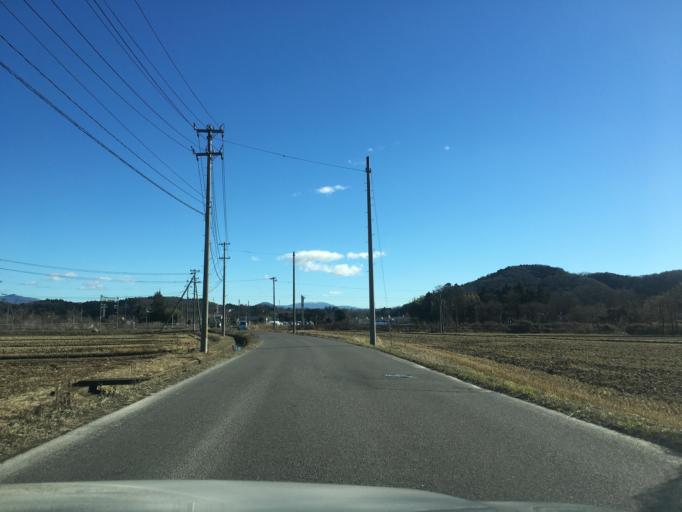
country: JP
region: Fukushima
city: Motomiya
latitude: 37.4850
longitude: 140.3874
